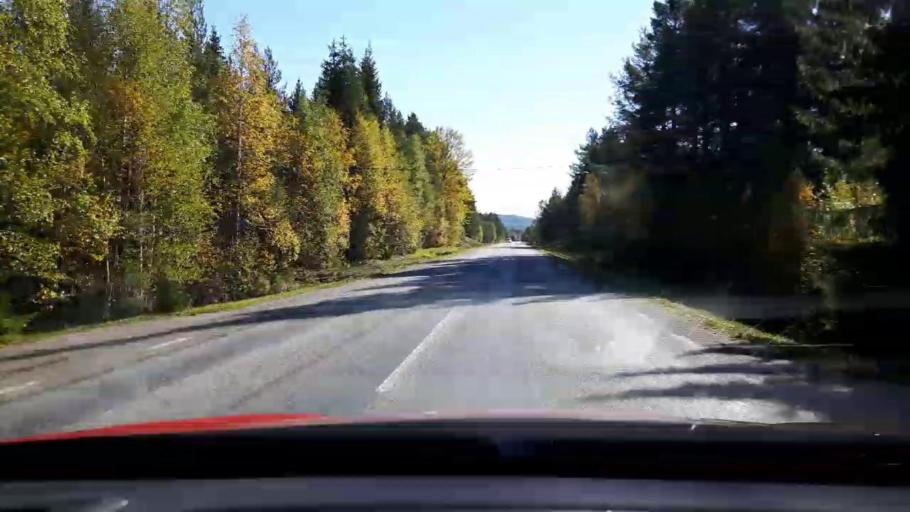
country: SE
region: Jaemtland
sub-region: Harjedalens Kommun
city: Sveg
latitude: 62.3575
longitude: 14.0122
